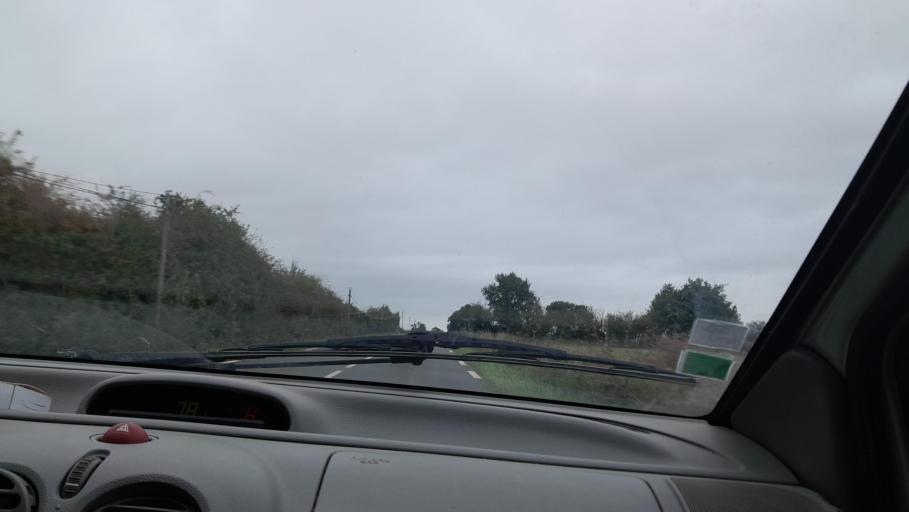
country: FR
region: Pays de la Loire
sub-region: Departement de la Loire-Atlantique
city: Saint-Mars-la-Jaille
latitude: 47.6301
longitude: -1.2007
